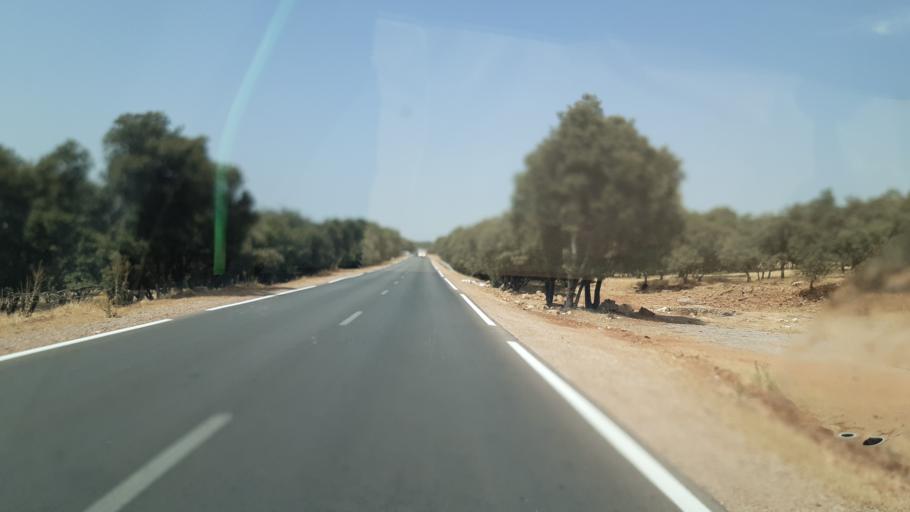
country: MA
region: Meknes-Tafilalet
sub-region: Ifrane
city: Ifrane
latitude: 33.6404
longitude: -5.0711
